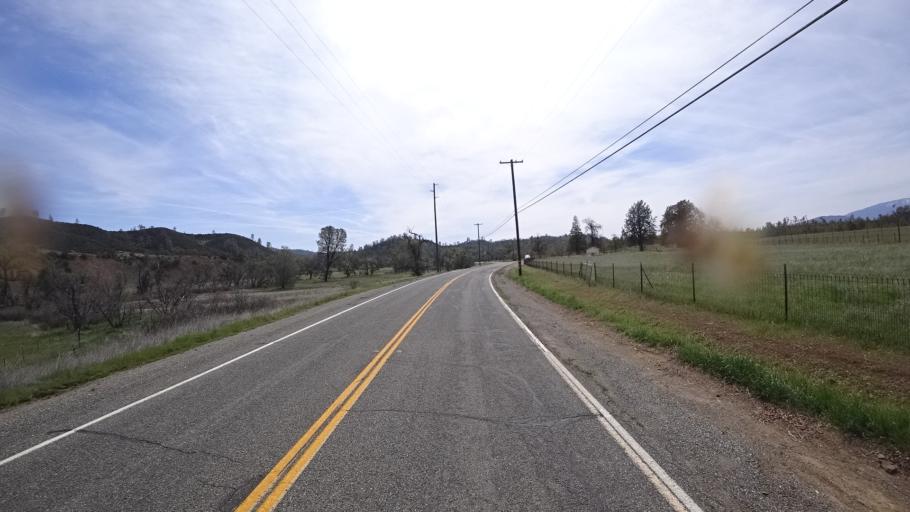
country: US
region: California
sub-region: Glenn County
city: Willows
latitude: 39.5928
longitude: -122.5413
